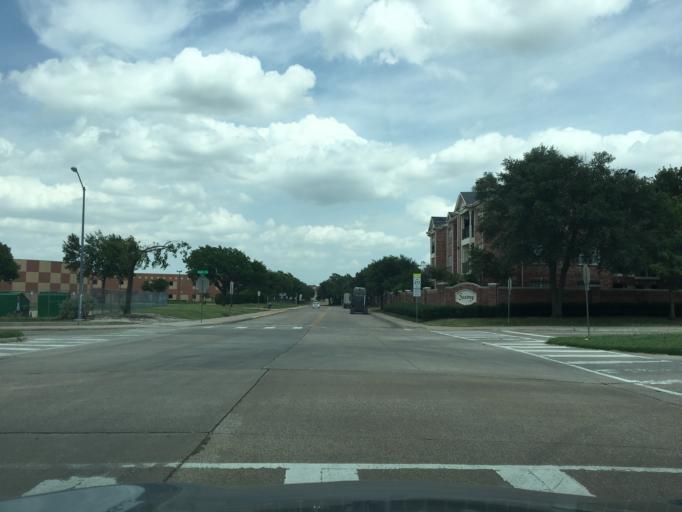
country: US
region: Texas
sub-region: Dallas County
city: Addison
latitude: 32.9468
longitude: -96.8194
